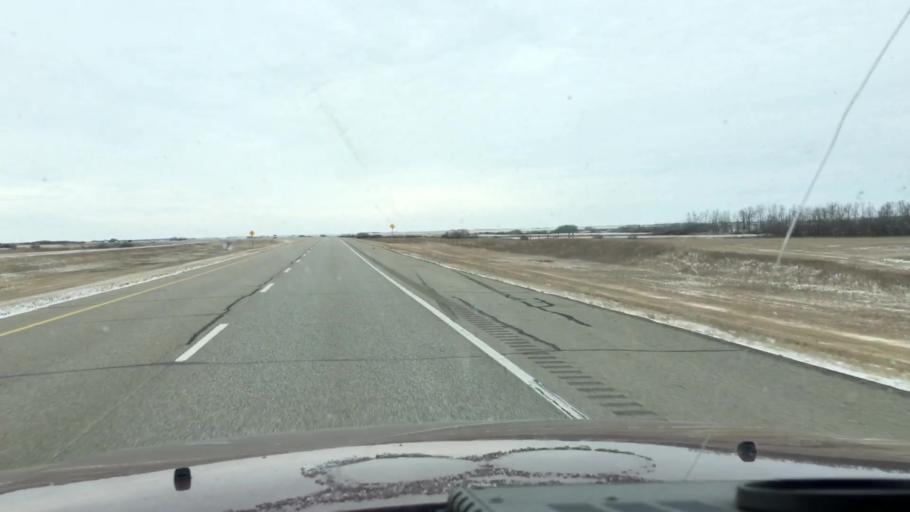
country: CA
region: Saskatchewan
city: Watrous
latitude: 51.3565
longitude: -106.1235
